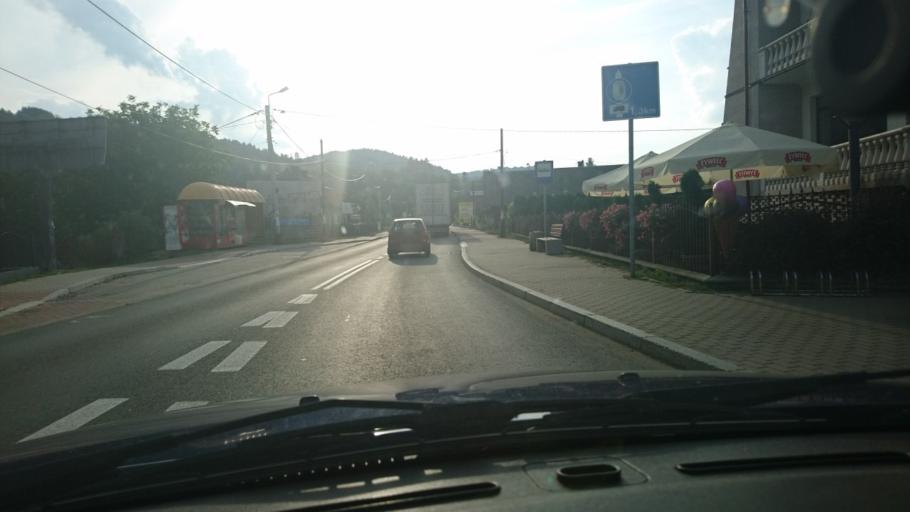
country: PL
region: Silesian Voivodeship
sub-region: Powiat zywiecki
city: Milowka
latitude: 49.5594
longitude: 19.0864
